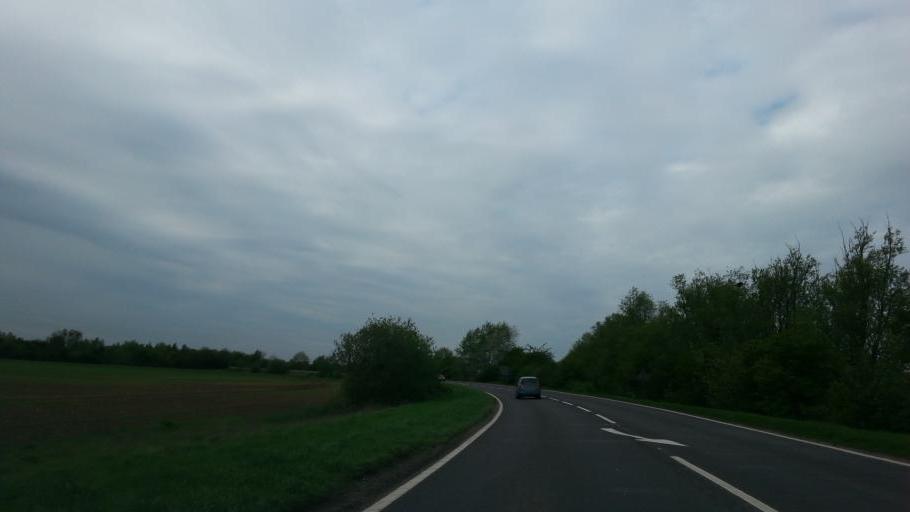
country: GB
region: England
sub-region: Cambridgeshire
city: March
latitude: 52.5176
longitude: 0.0909
